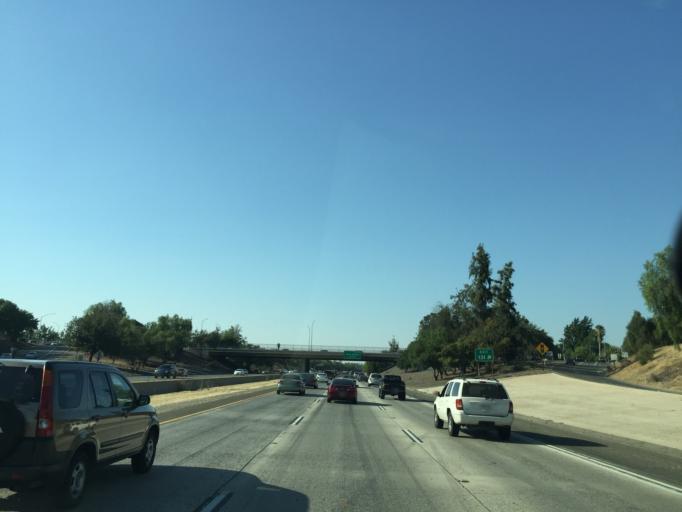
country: US
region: California
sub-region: Fresno County
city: Fresno
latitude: 36.7920
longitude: -119.7844
